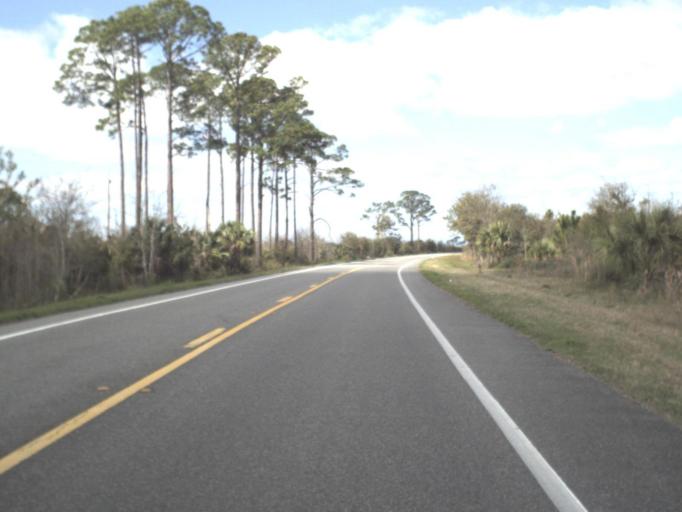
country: US
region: Florida
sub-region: Franklin County
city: Apalachicola
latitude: 29.7184
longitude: -85.0607
